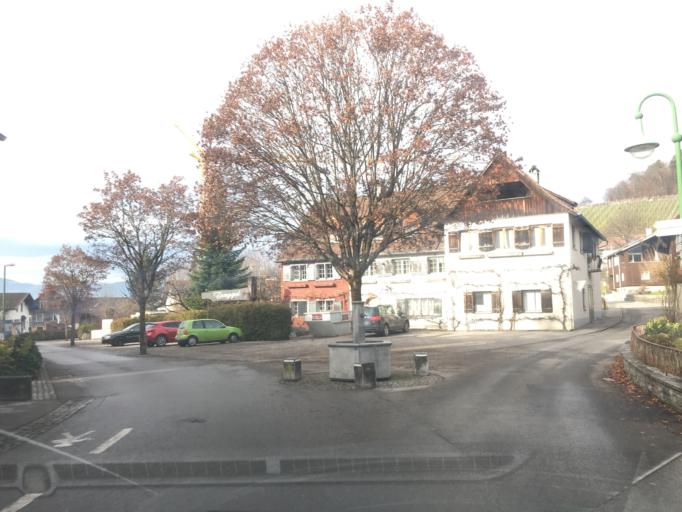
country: AT
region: Vorarlberg
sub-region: Politischer Bezirk Feldkirch
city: Rothis
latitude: 47.2931
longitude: 9.6573
